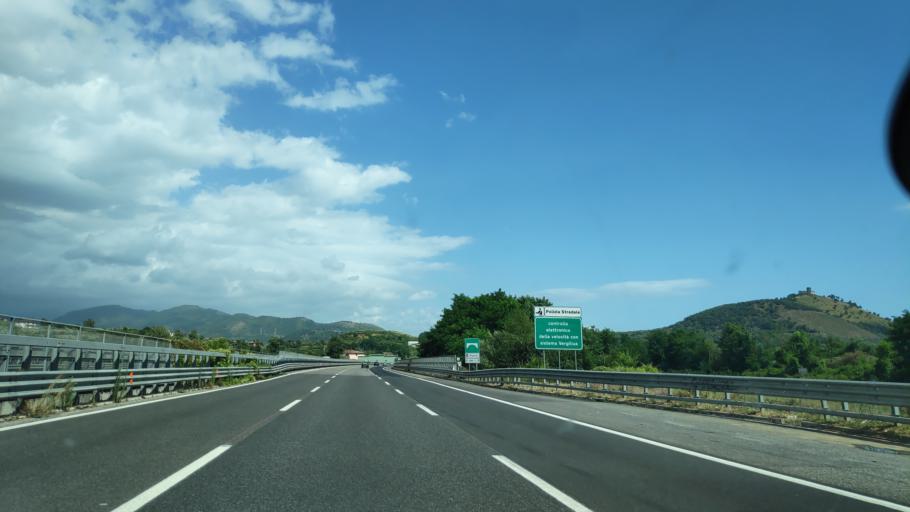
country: IT
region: Campania
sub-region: Provincia di Salerno
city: San Mango Piemonte
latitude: 40.6865
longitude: 14.8479
